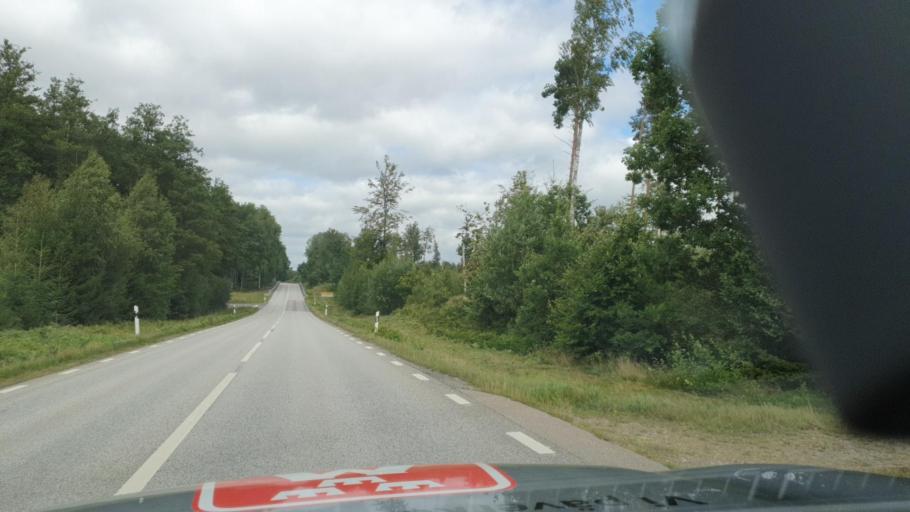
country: SE
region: Blekinge
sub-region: Karlskrona Kommun
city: Rodeby
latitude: 56.2968
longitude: 15.5836
